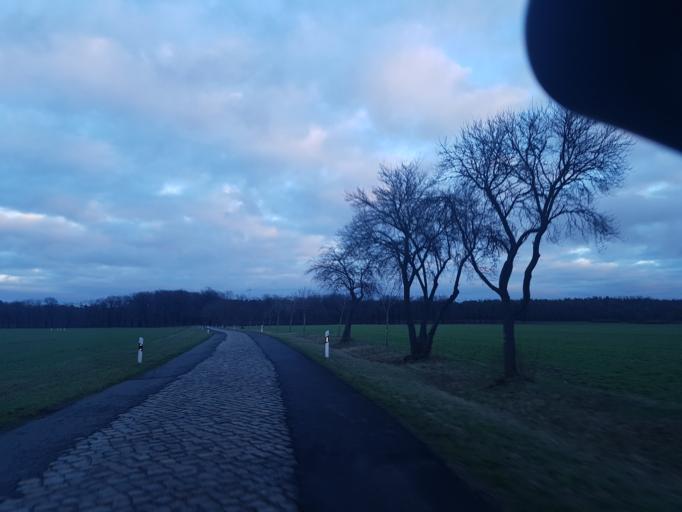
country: DE
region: Brandenburg
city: Muhlberg
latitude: 51.4752
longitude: 13.2170
